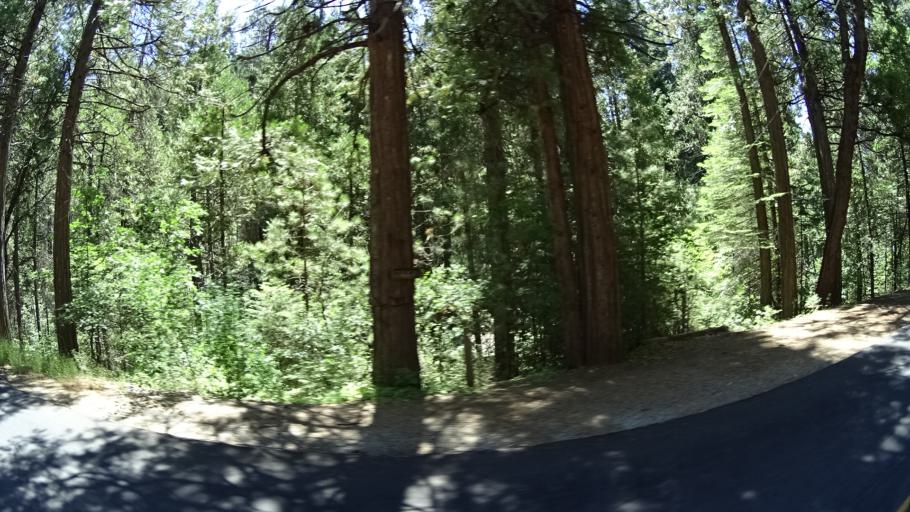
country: US
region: California
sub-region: Calaveras County
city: Arnold
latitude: 38.2315
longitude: -120.3540
